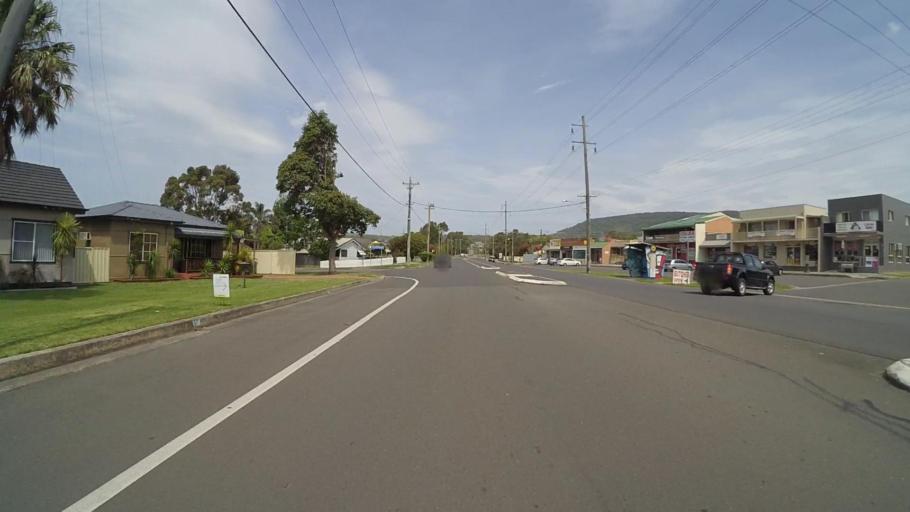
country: AU
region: New South Wales
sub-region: Shellharbour
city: Albion Park Rail
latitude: -34.5786
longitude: 150.7773
